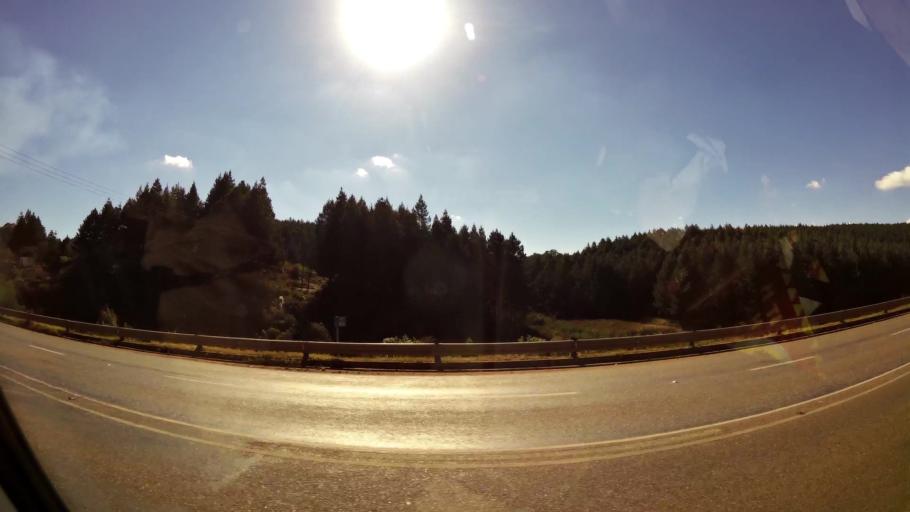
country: ZA
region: Limpopo
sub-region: Capricorn District Municipality
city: Mankoeng
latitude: -23.9405
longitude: 29.9439
